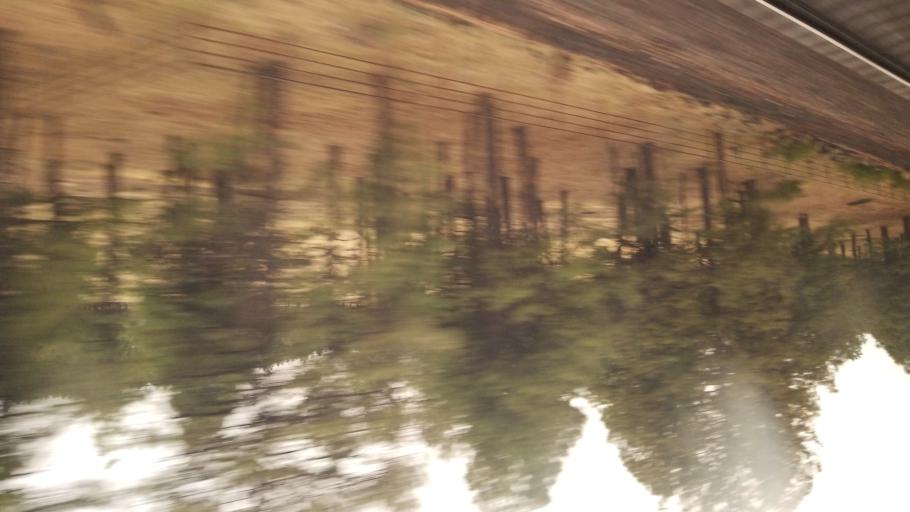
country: US
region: Arizona
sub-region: Coconino County
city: Parks
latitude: 35.2345
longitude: -112.0059
